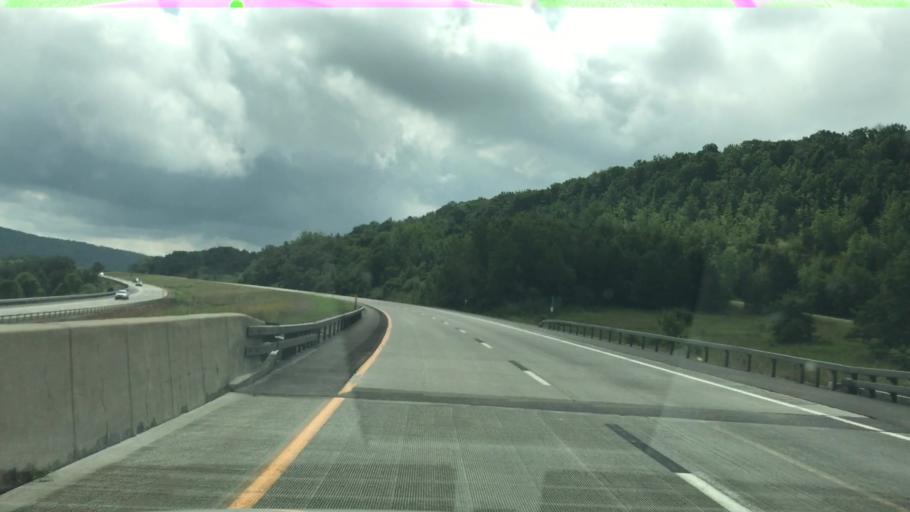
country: US
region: New York
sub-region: Steuben County
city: Wayland
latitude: 42.5151
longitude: -77.5370
